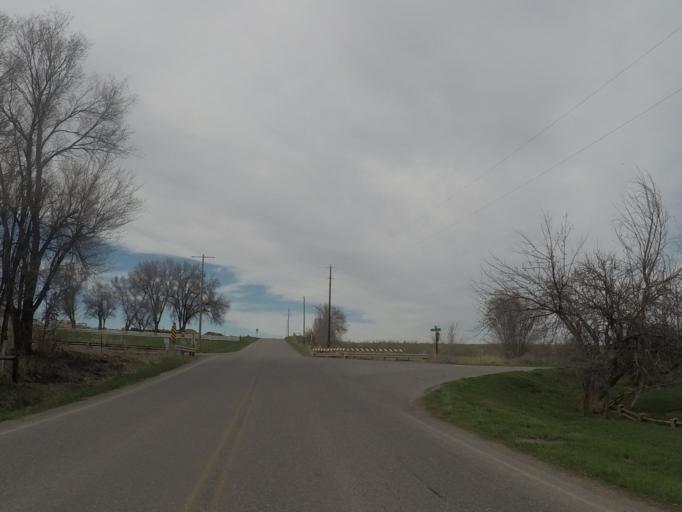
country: US
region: Montana
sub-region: Yellowstone County
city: Laurel
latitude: 45.7111
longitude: -108.6587
